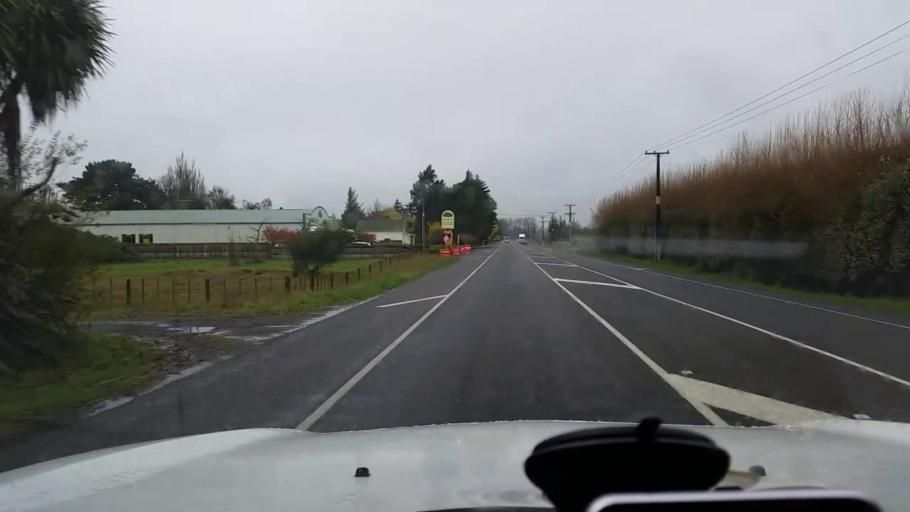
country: NZ
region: Wellington
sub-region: Masterton District
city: Masterton
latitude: -41.0720
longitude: 175.4698
